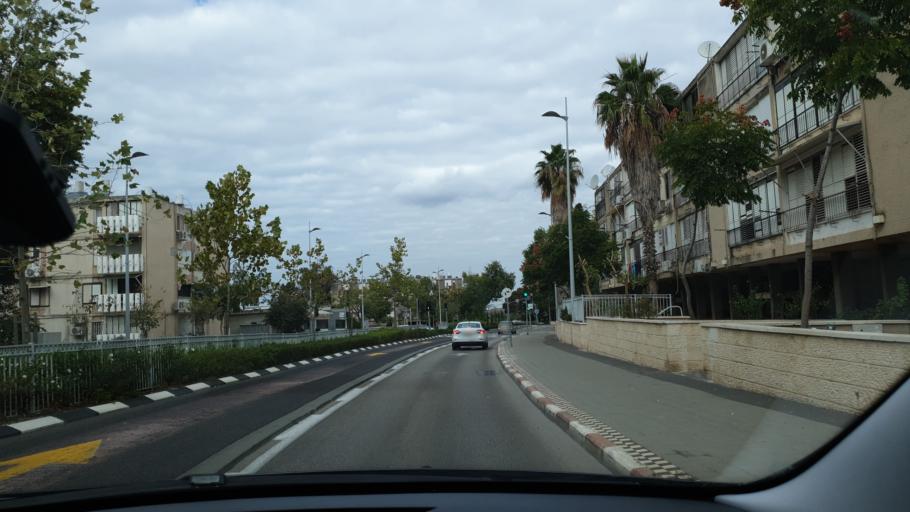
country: IL
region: Haifa
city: Qiryat Ata
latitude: 32.8150
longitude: 35.1136
